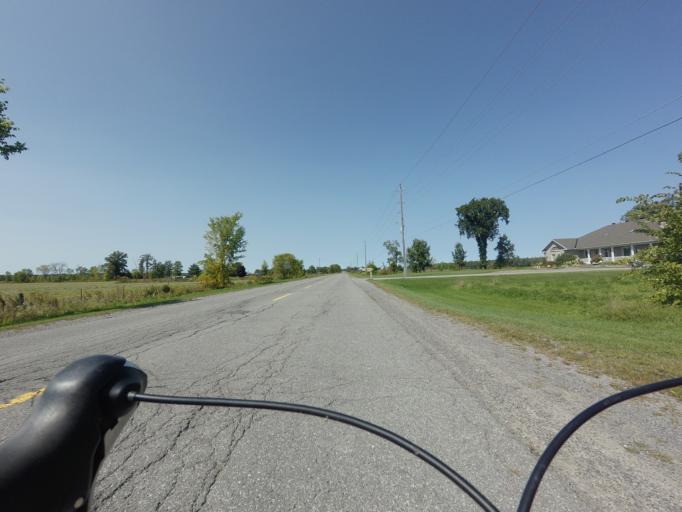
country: CA
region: Ontario
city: Arnprior
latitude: 45.4780
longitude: -76.1195
